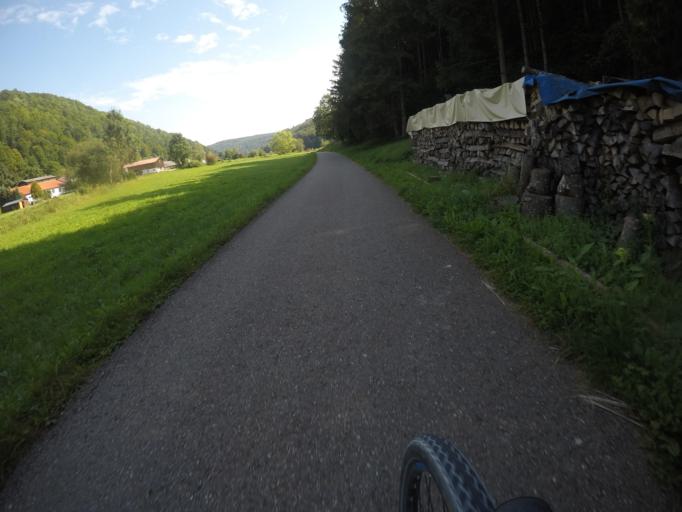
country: DE
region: Baden-Wuerttemberg
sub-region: Tuebingen Region
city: Mehrstetten
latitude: 48.3703
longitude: 9.6405
